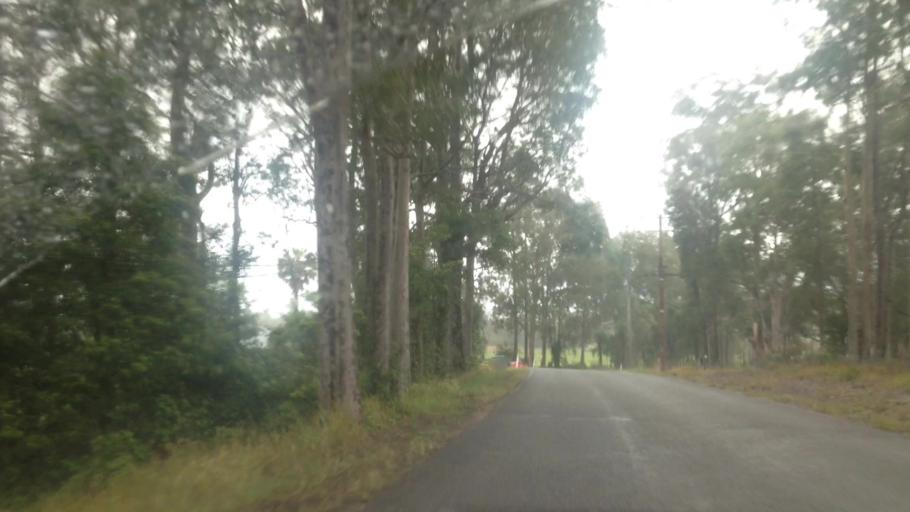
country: AU
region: New South Wales
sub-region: Wyong Shire
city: Little Jilliby
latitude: -33.2133
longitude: 151.3715
